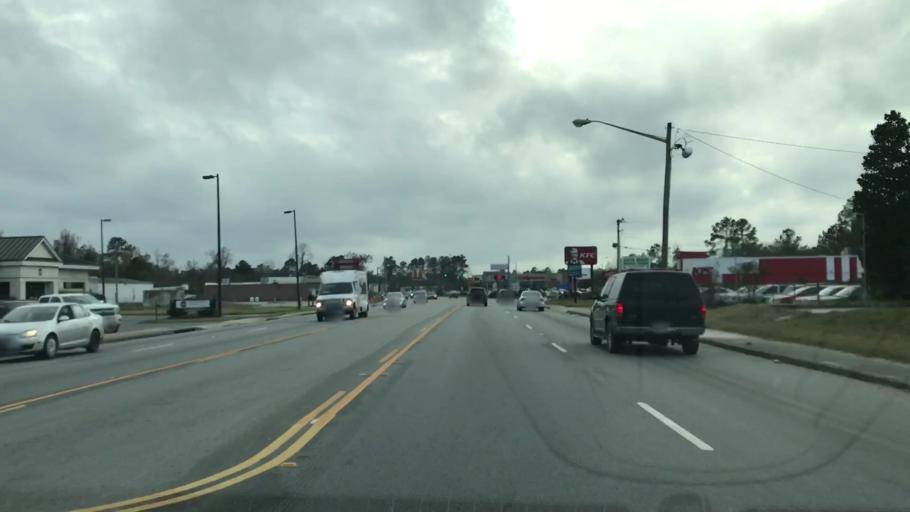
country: US
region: South Carolina
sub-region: Berkeley County
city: Moncks Corner
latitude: 33.2036
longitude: -79.9884
